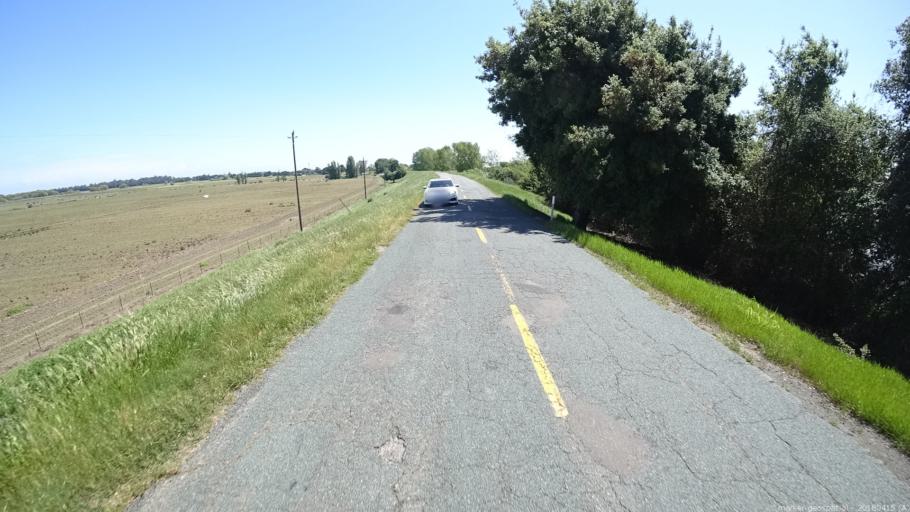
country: US
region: California
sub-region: Solano County
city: Rio Vista
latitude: 38.1654
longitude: -121.6189
